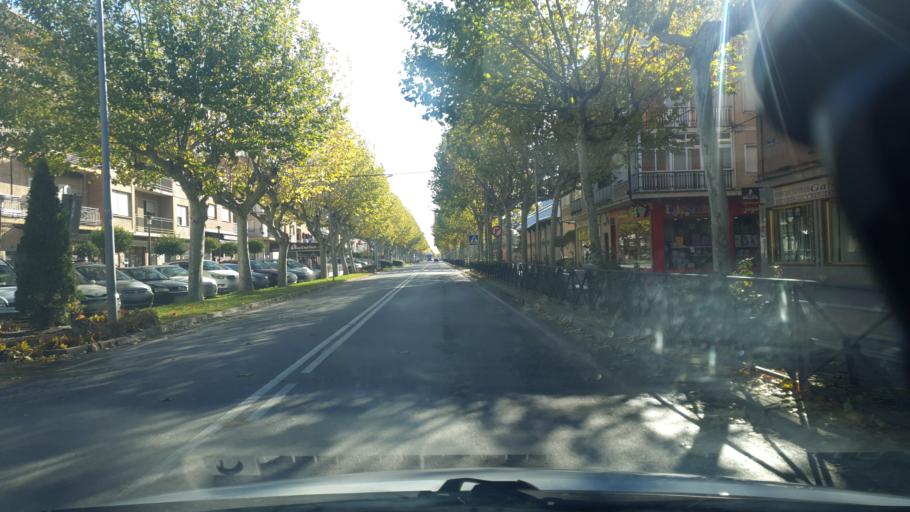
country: ES
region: Castille and Leon
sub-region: Provincia de Avila
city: Arevalo
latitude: 41.0572
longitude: -4.7161
